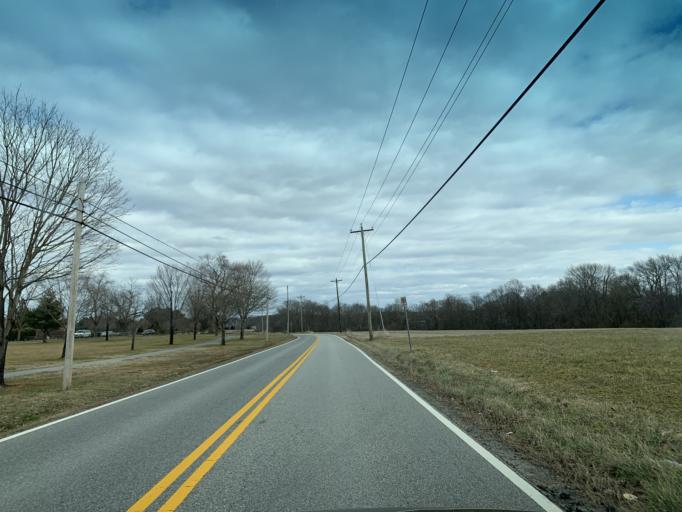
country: US
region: Maryland
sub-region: Queen Anne's County
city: Centreville
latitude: 39.0275
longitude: -76.1107
